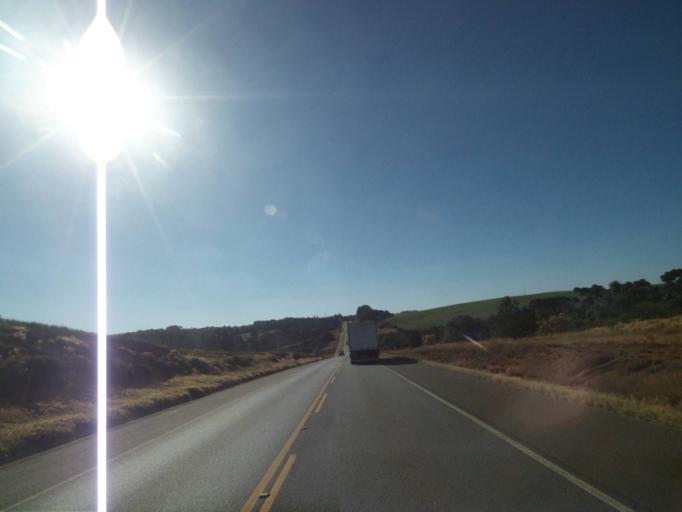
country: BR
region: Parana
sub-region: Tibagi
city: Tibagi
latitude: -24.5384
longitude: -50.4469
